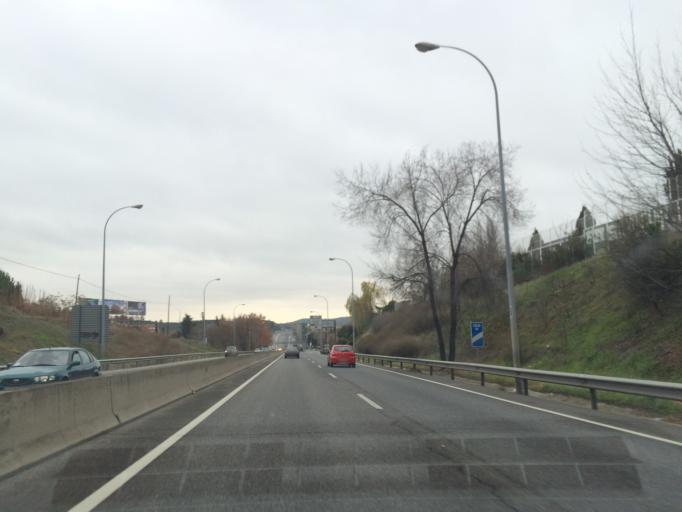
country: ES
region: Madrid
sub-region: Provincia de Madrid
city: Moncloa-Aravaca
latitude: 40.4589
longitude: -3.7698
